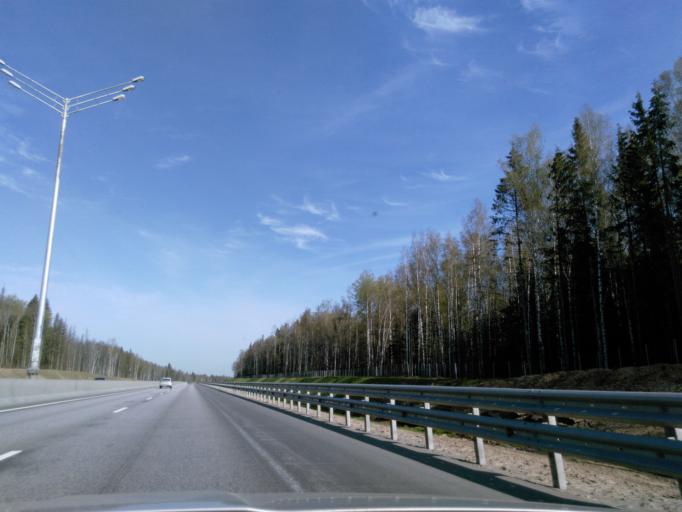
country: RU
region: Moskovskaya
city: Mendeleyevo
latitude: 56.0664
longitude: 37.2295
